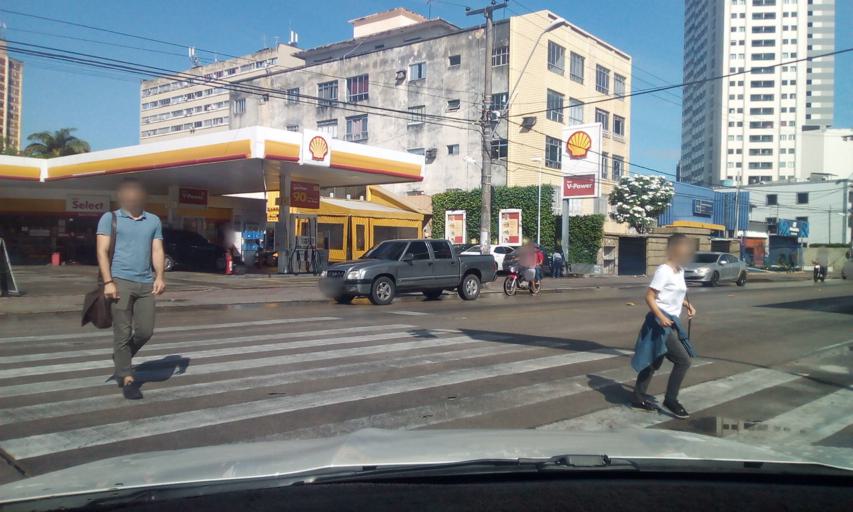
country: BR
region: Pernambuco
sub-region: Recife
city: Recife
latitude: -8.0565
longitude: -34.8926
